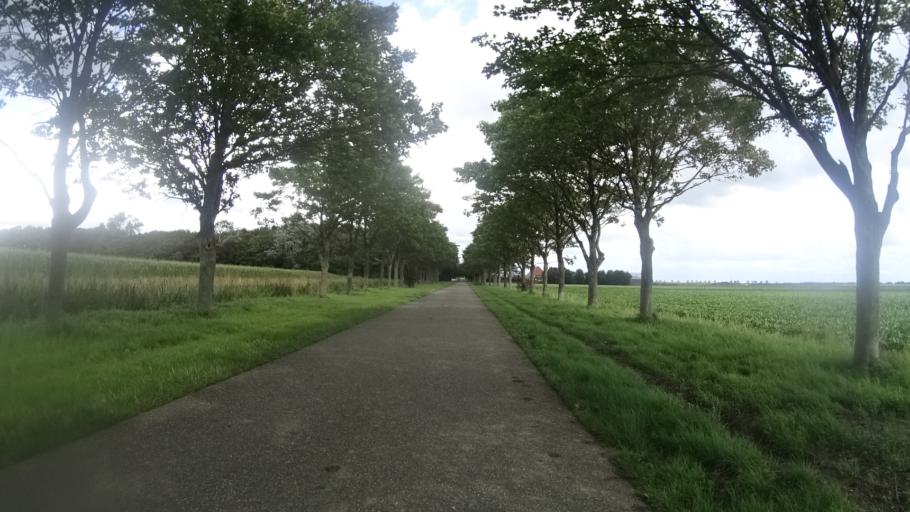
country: NL
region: North Holland
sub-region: Gemeente Hollands Kroon
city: Den Oever
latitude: 52.8892
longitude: 4.9624
